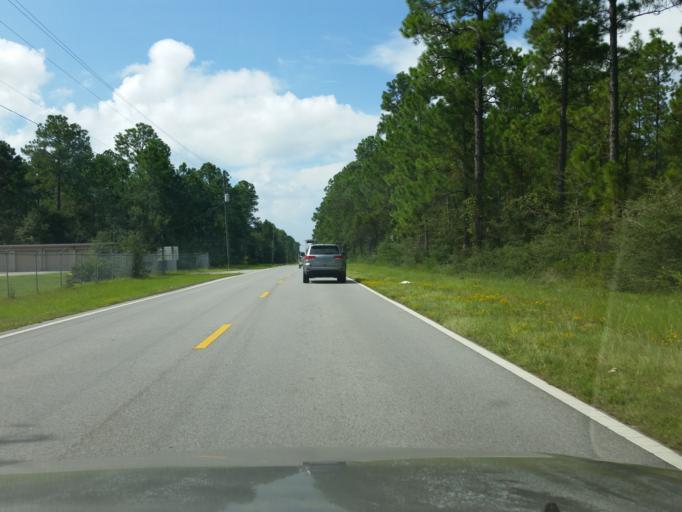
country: US
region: Florida
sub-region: Escambia County
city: Myrtle Grove
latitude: 30.3378
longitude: -87.4034
